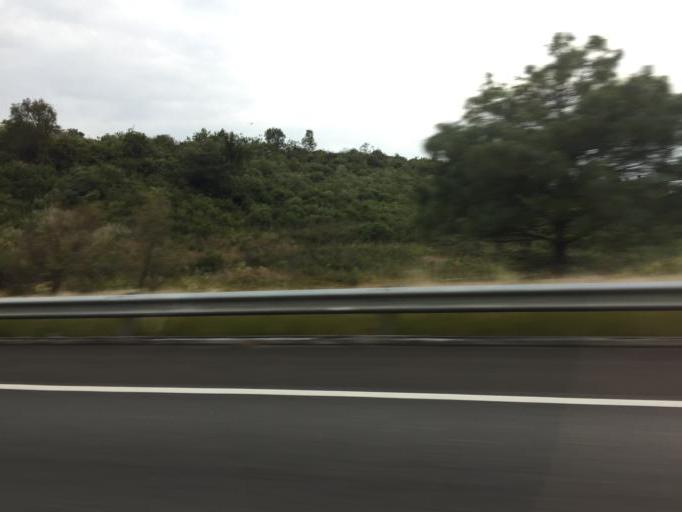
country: MX
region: Michoacan
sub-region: Puruandiro
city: San Lorenzo
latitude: 19.9530
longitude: -101.6531
